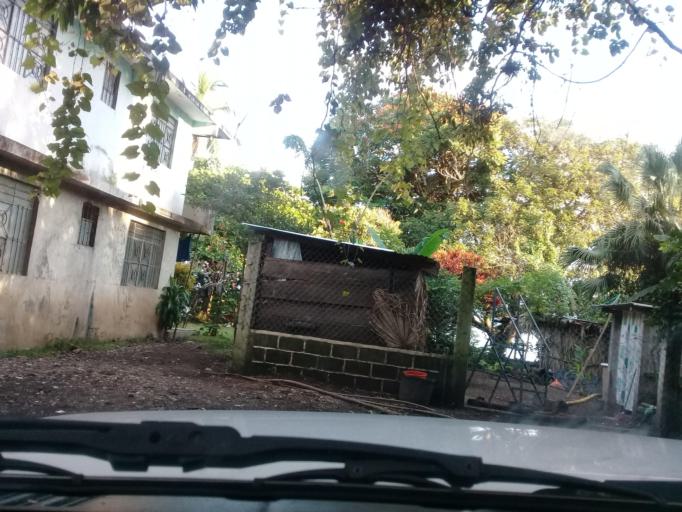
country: MX
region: Veracruz
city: Catemaco
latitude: 18.4290
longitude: -95.0920
